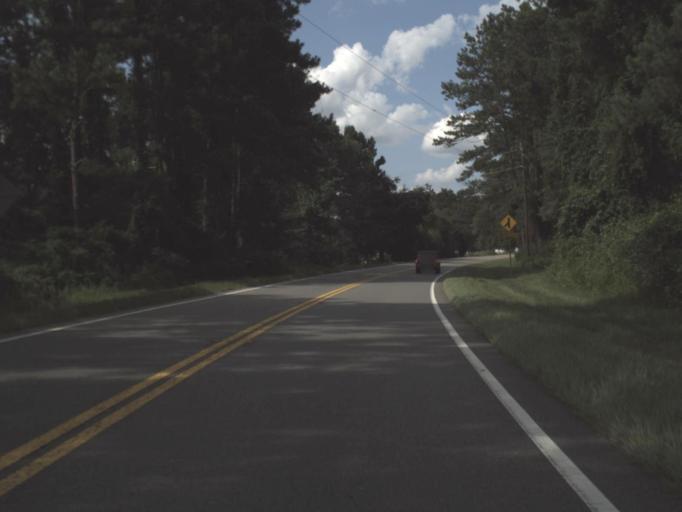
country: US
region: Florida
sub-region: Madison County
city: Madison
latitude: 30.4011
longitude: -83.6521
